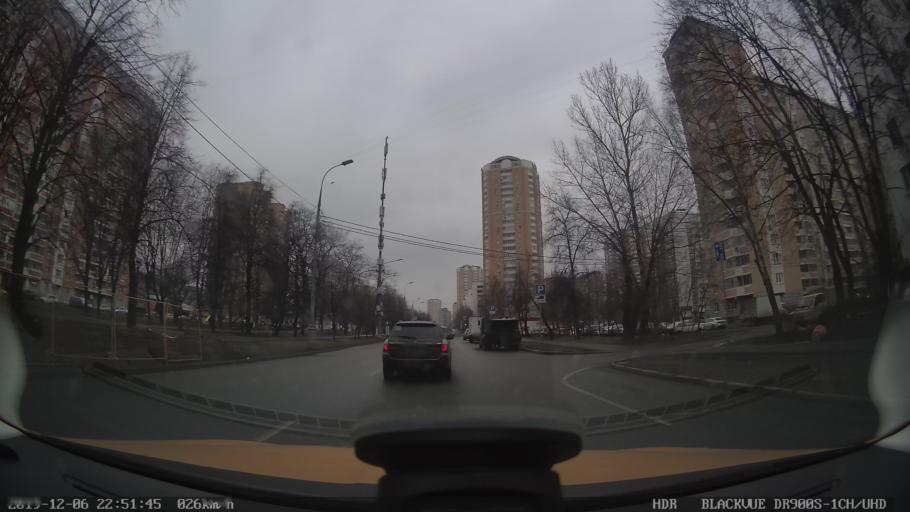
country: RU
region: Moskovskaya
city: Vostochnoe Degunino
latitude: 55.8666
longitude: 37.5586
